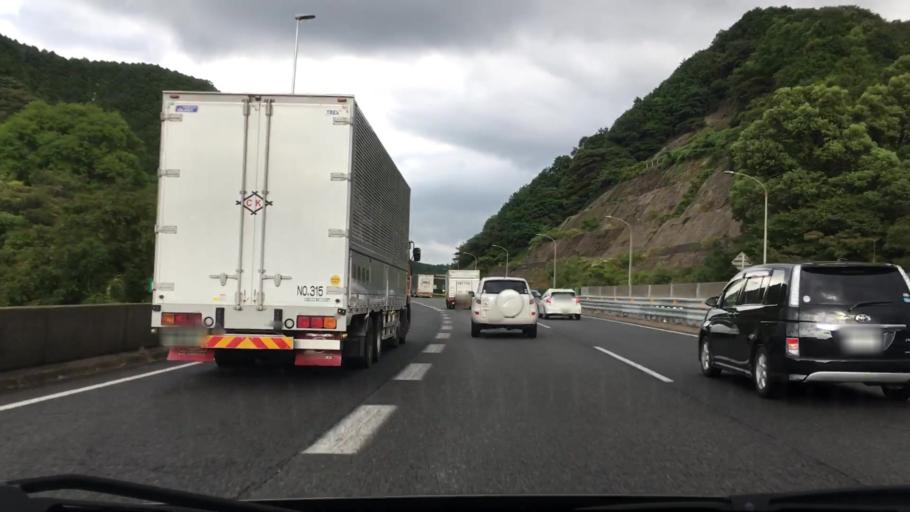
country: JP
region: Fukuoka
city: Nishifukuma
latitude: 33.7494
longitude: 130.5503
